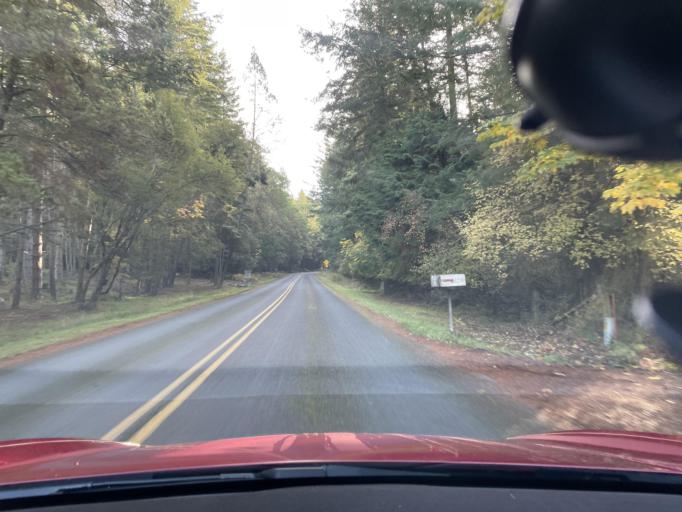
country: US
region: Washington
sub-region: San Juan County
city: Friday Harbor
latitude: 48.5507
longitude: -123.1625
